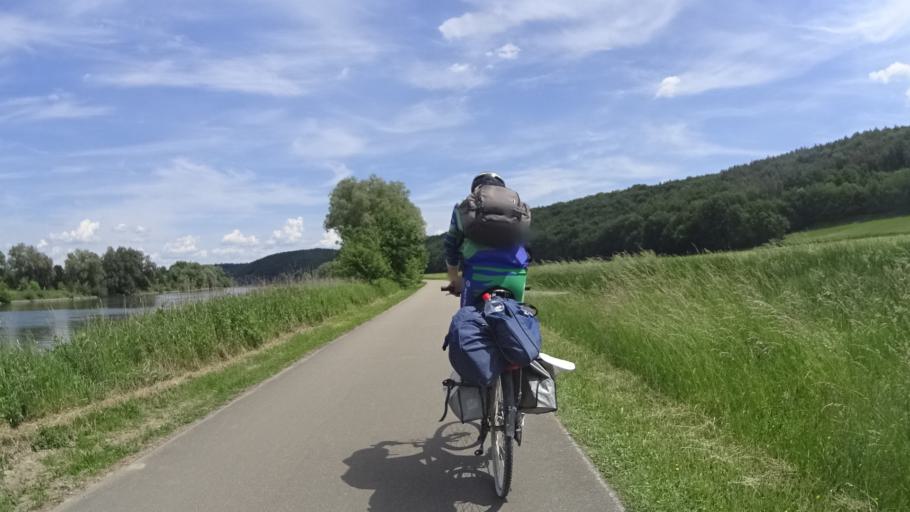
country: DE
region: Bavaria
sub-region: Upper Palatinate
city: Sinzing
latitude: 48.9685
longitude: 12.0212
